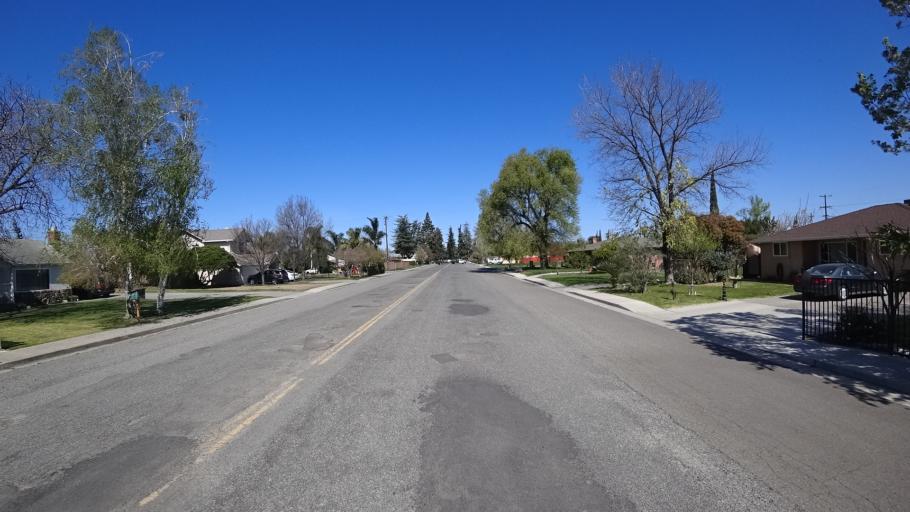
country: US
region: California
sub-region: Glenn County
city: Hamilton City
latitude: 39.7428
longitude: -122.0170
